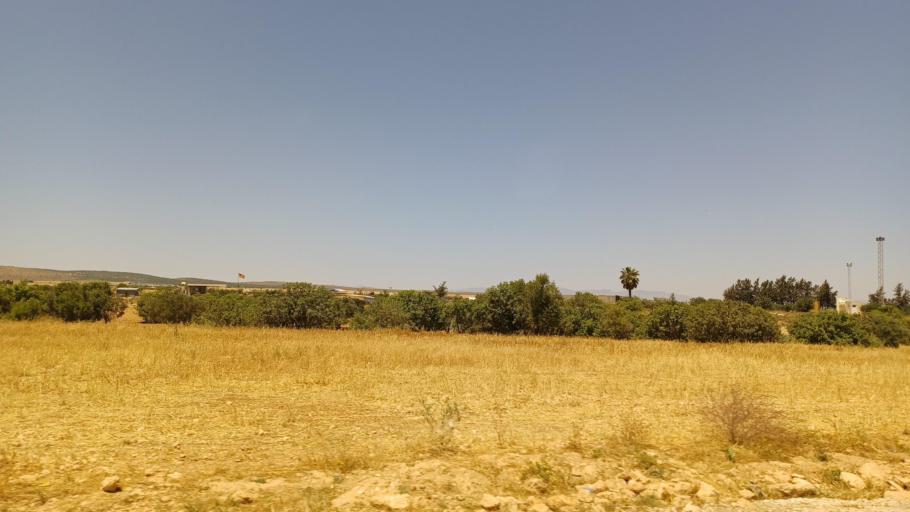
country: CY
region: Larnaka
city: Pyla
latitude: 35.0236
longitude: 33.7022
